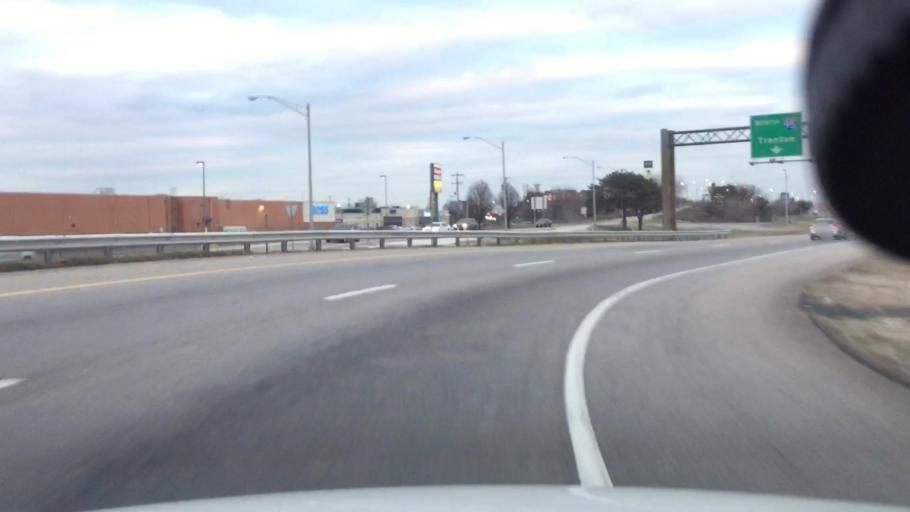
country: US
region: New Jersey
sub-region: Camden County
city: Camden
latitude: 39.9116
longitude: -75.1576
